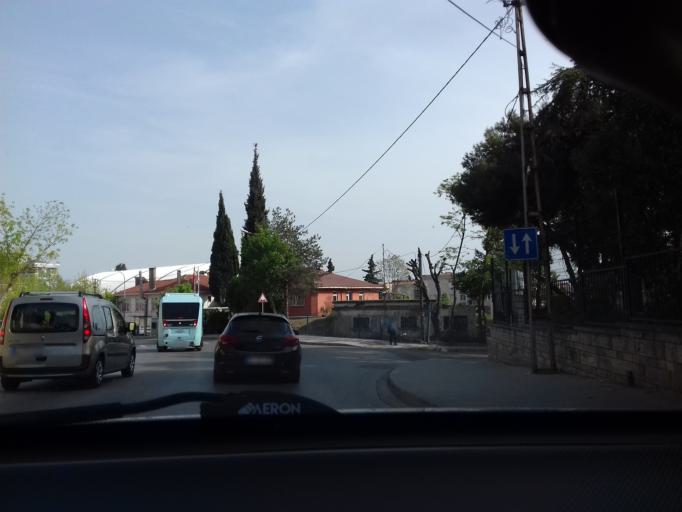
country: TR
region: Istanbul
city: Pendik
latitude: 40.9156
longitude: 29.2215
